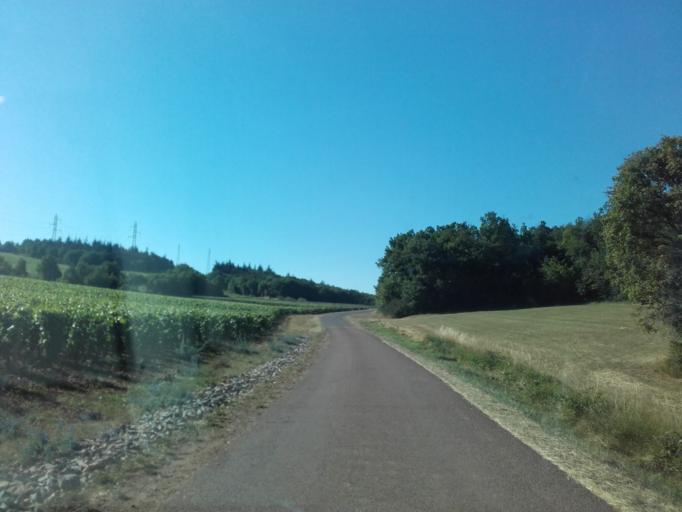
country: FR
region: Bourgogne
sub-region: Departement de Saone-et-Loire
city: Rully
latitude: 46.8475
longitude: 4.7389
